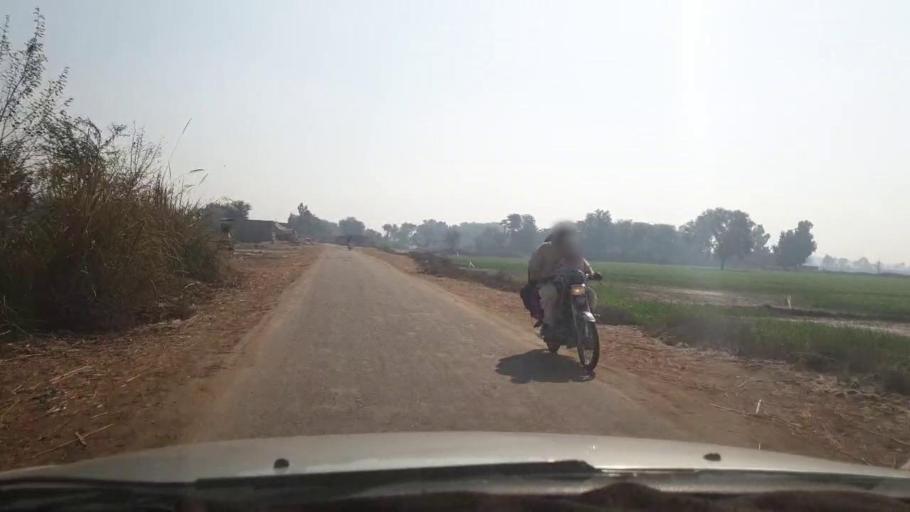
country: PK
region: Sindh
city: Khanpur
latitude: 27.7308
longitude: 69.5143
